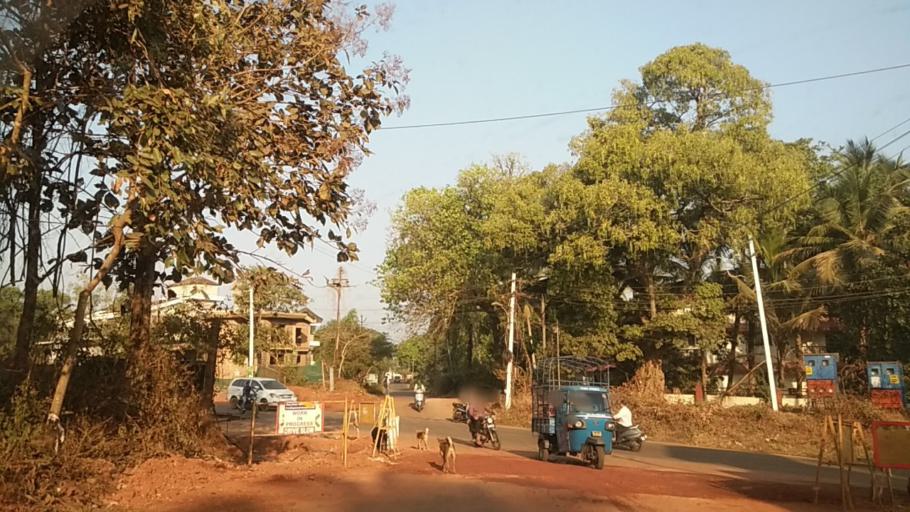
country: IN
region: Goa
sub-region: South Goa
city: Benaulim
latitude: 15.2787
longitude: 73.9343
